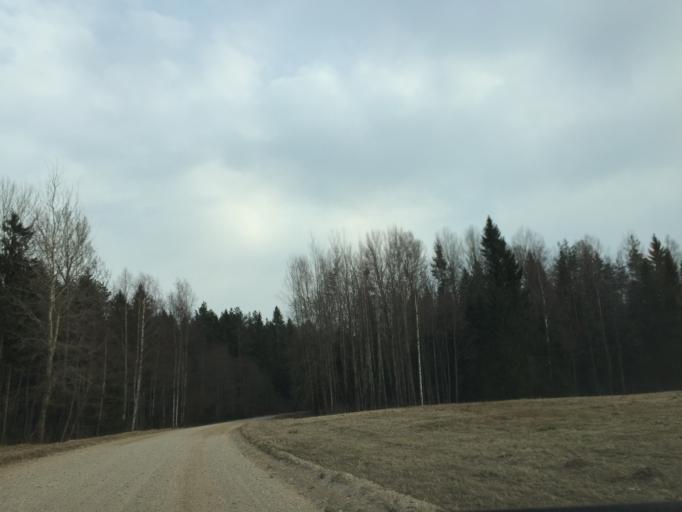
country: LV
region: Priekuli
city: Priekuli
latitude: 57.2029
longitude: 25.4353
